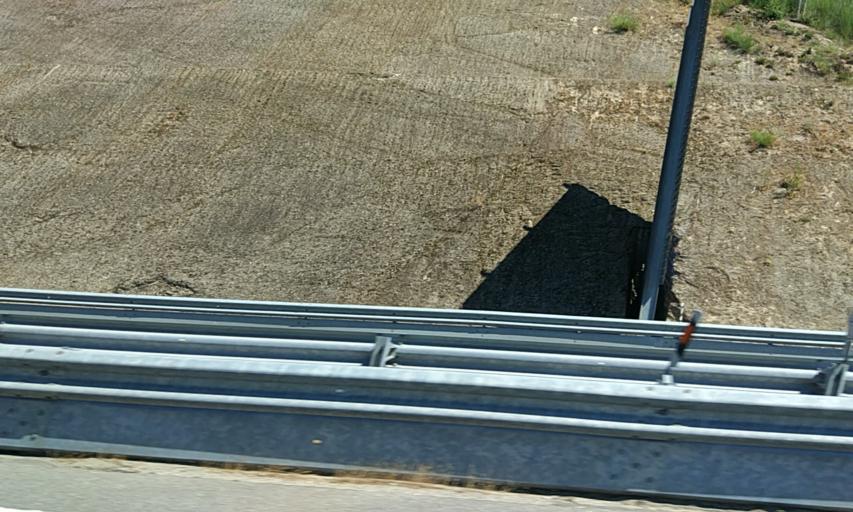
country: PT
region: Porto
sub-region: Amarante
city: Amarante
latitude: 41.2596
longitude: -8.0433
